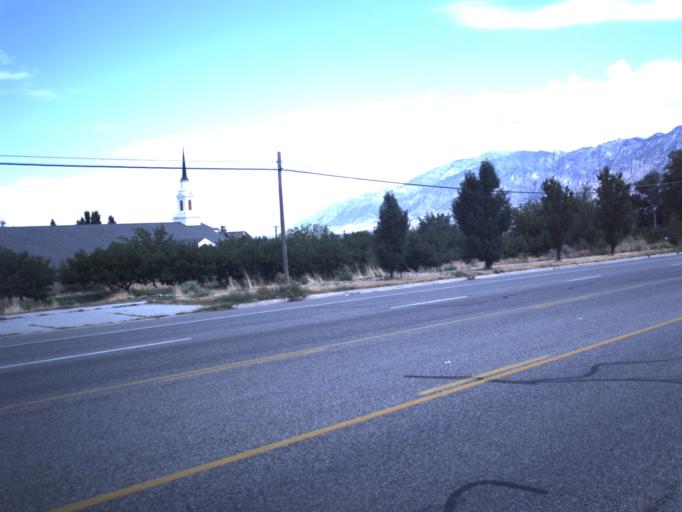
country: US
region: Utah
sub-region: Box Elder County
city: Perry
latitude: 41.4675
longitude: -112.0313
